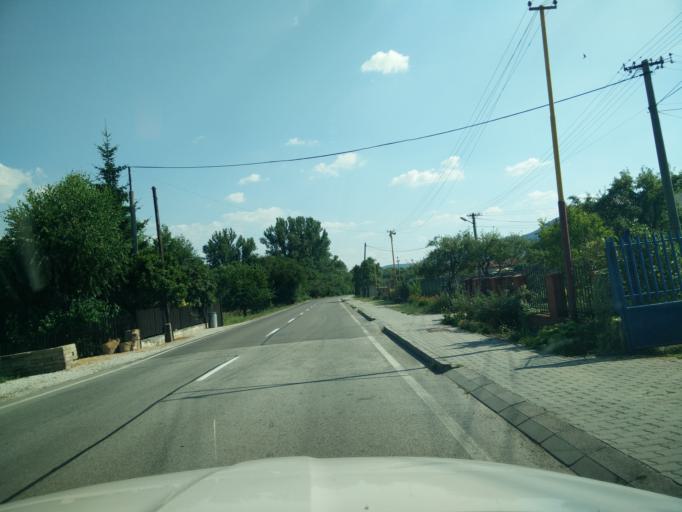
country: SK
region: Nitriansky
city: Bojnice
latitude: 48.8210
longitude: 18.4802
